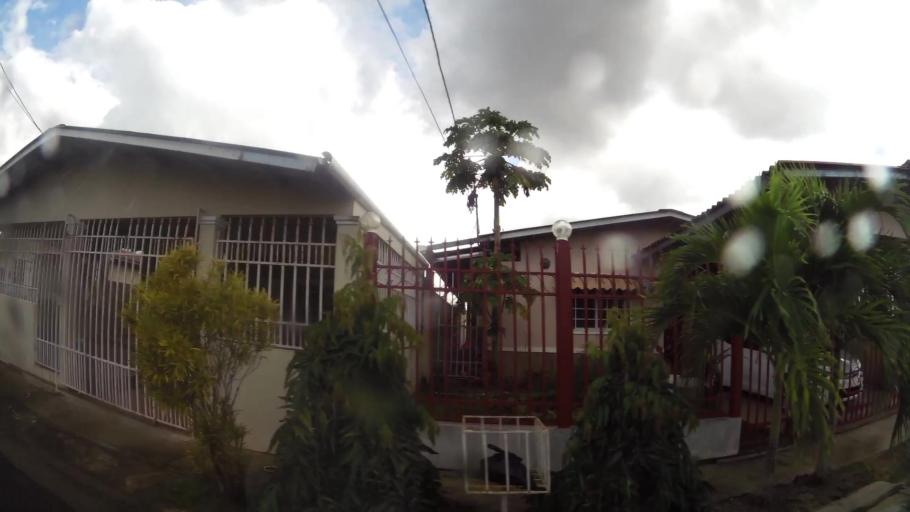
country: PA
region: Panama
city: Nuevo Arraijan
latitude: 8.9404
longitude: -79.7367
